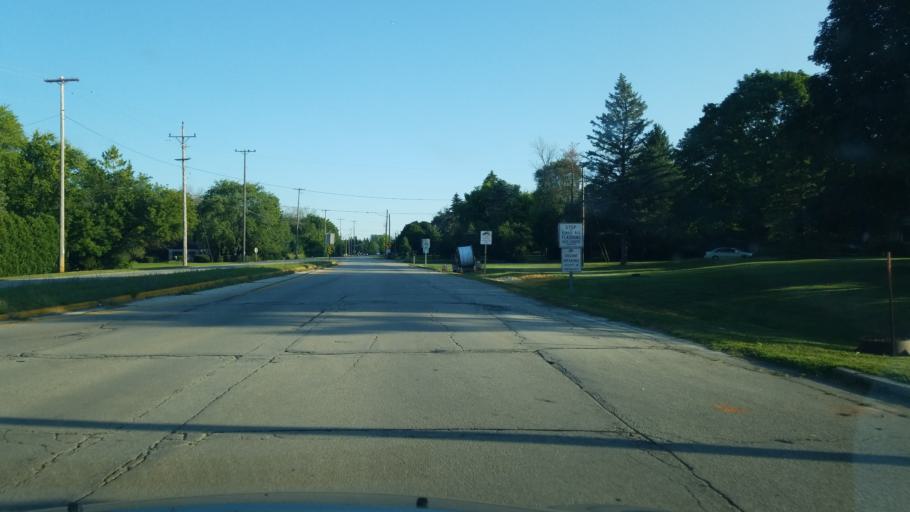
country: US
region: Wisconsin
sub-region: Milwaukee County
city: Brown Deer
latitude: 43.1925
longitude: -87.9646
